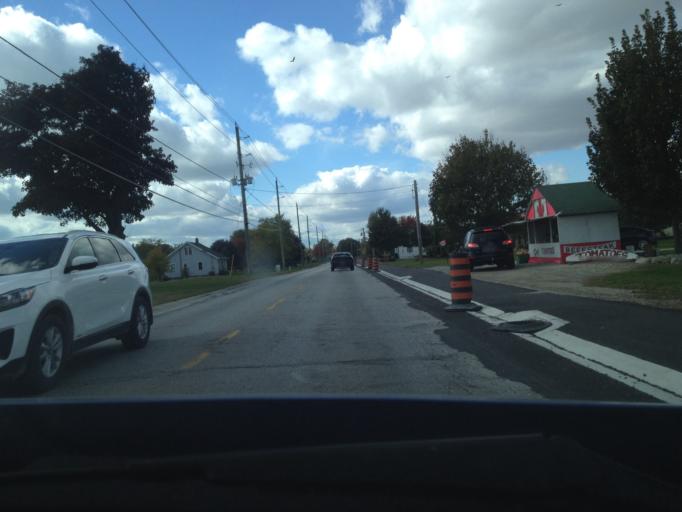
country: CA
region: Ontario
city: Amherstburg
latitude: 42.0348
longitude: -82.6252
